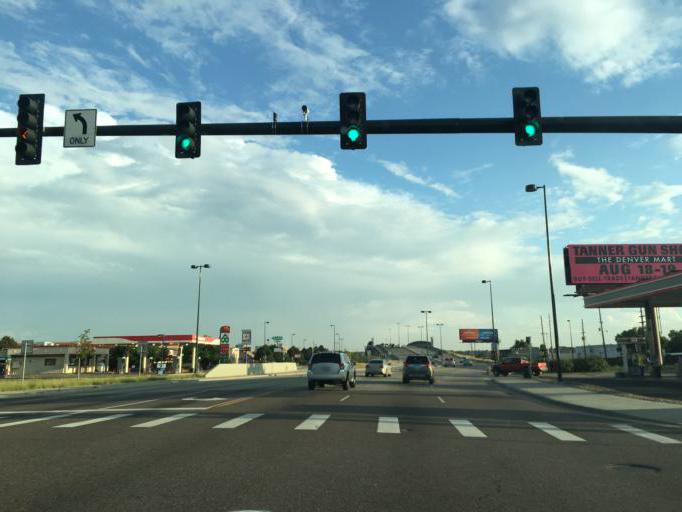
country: US
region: Colorado
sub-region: Adams County
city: Aurora
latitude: 39.7710
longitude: -104.8472
